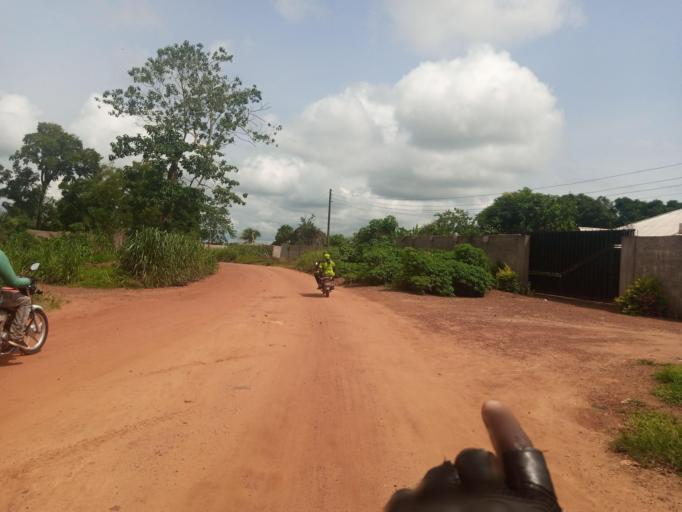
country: SL
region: Southern Province
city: Bo
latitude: 7.9688
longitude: -11.7496
